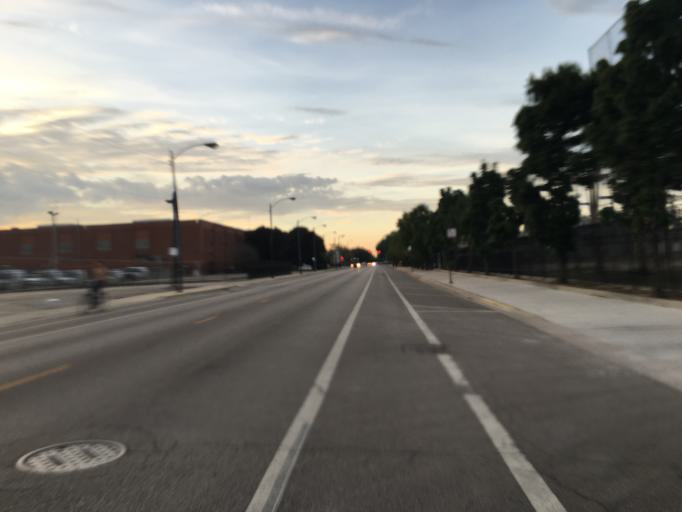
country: US
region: Illinois
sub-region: Cook County
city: Lincolnwood
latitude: 41.9445
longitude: -87.6980
